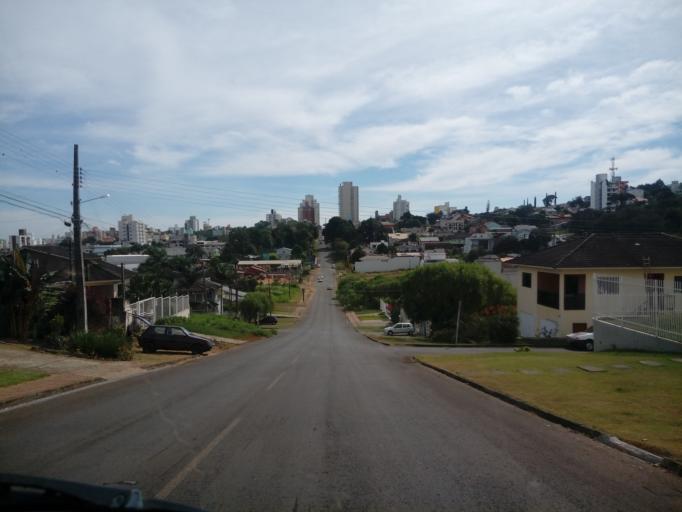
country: BR
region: Santa Catarina
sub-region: Chapeco
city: Chapeco
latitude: -27.1185
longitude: -52.6141
